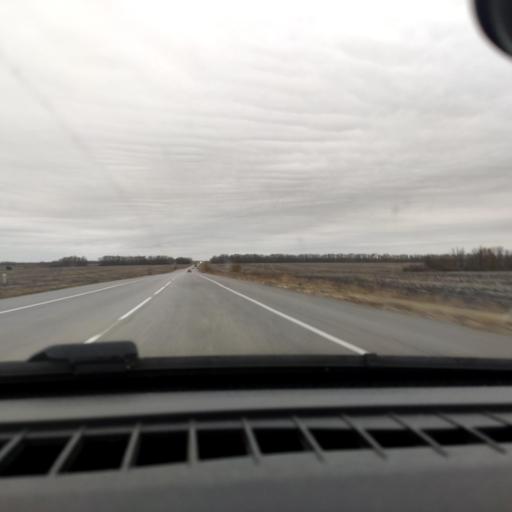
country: RU
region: Voronezj
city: Strelitsa
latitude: 51.4966
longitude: 38.9647
